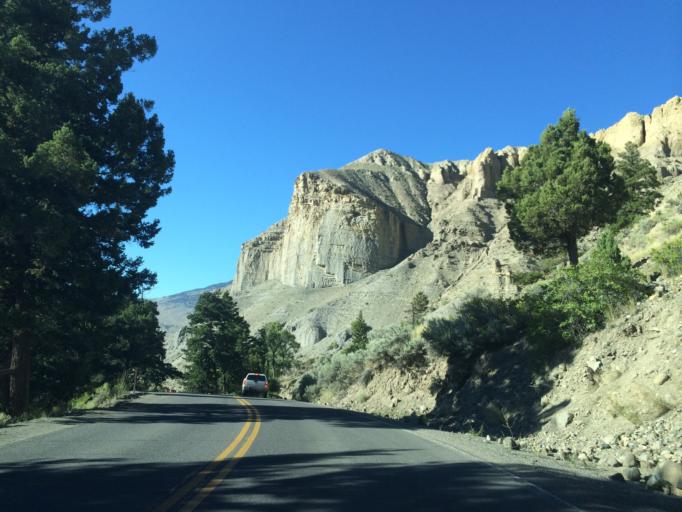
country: US
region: Montana
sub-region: Gallatin County
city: West Yellowstone
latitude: 45.0041
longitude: -110.6918
